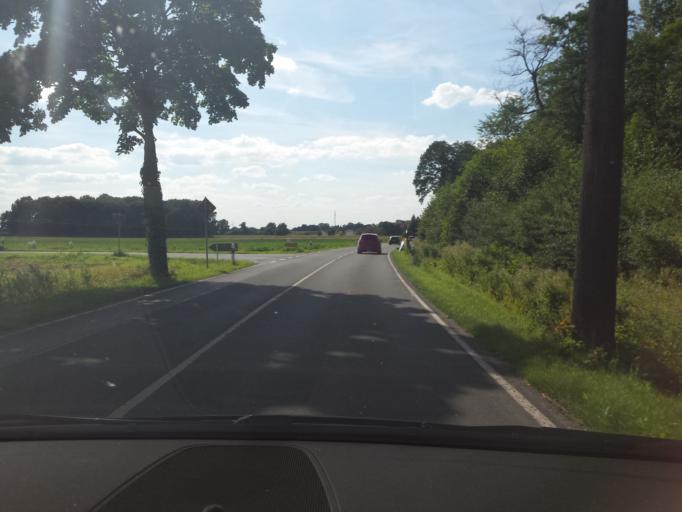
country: DE
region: North Rhine-Westphalia
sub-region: Regierungsbezirk Arnsberg
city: Lippstadt
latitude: 51.6535
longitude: 8.2986
